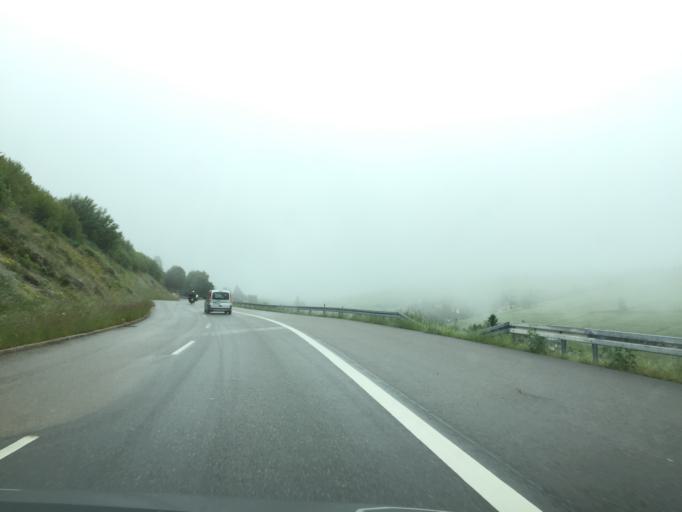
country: DE
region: Baden-Wuerttemberg
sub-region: Freiburg Region
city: Todtnau
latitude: 47.8463
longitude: 7.9382
